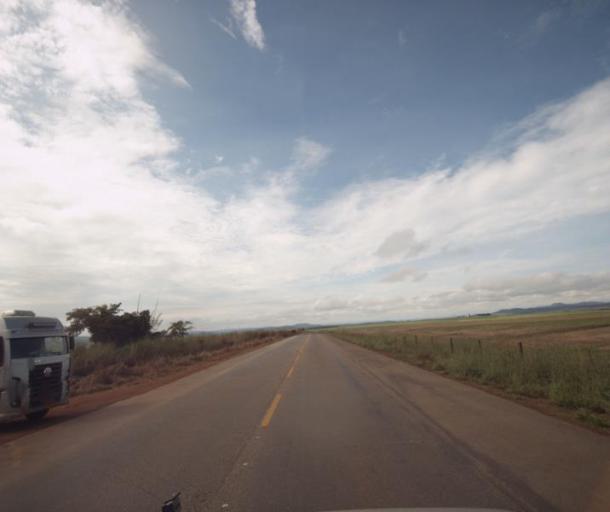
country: BR
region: Goias
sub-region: Padre Bernardo
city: Padre Bernardo
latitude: -15.3839
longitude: -48.6419
